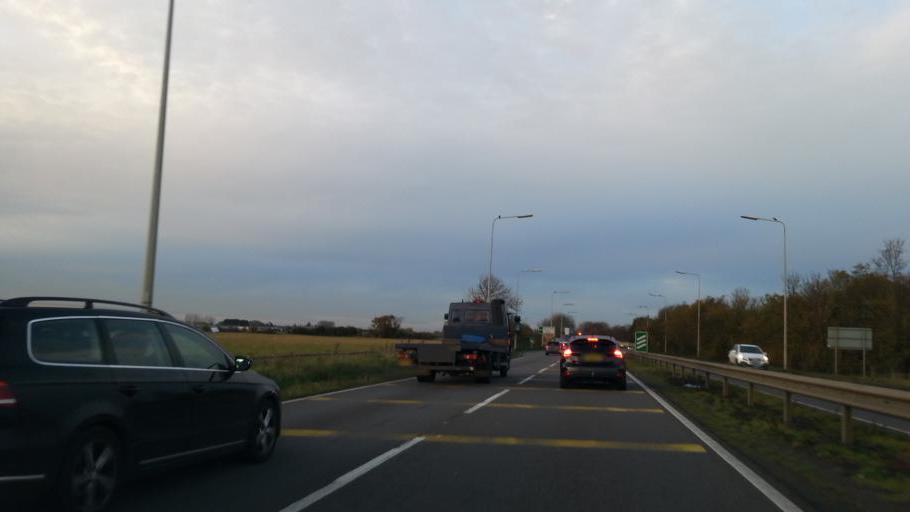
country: GB
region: England
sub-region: Central Bedfordshire
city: Biggleswade
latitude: 52.0890
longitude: -0.2743
